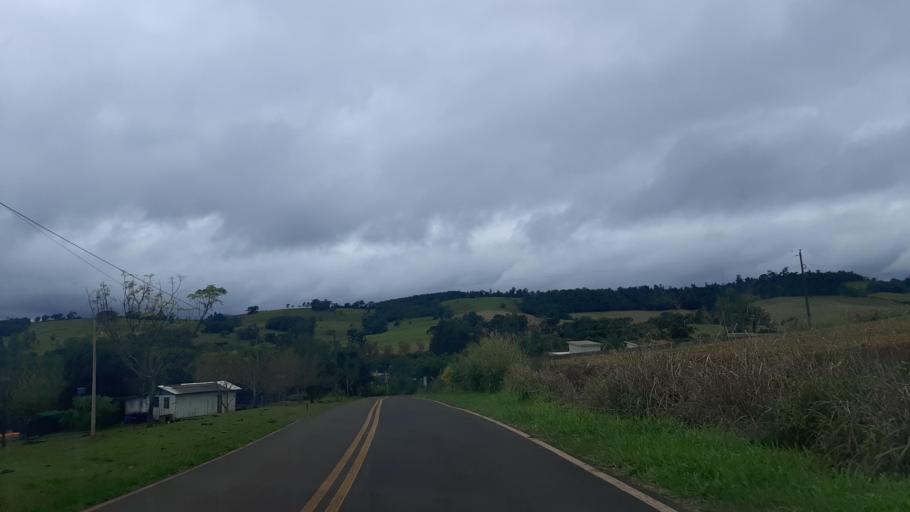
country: BR
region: Parana
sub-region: Ampere
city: Ampere
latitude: -25.9736
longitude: -53.4439
